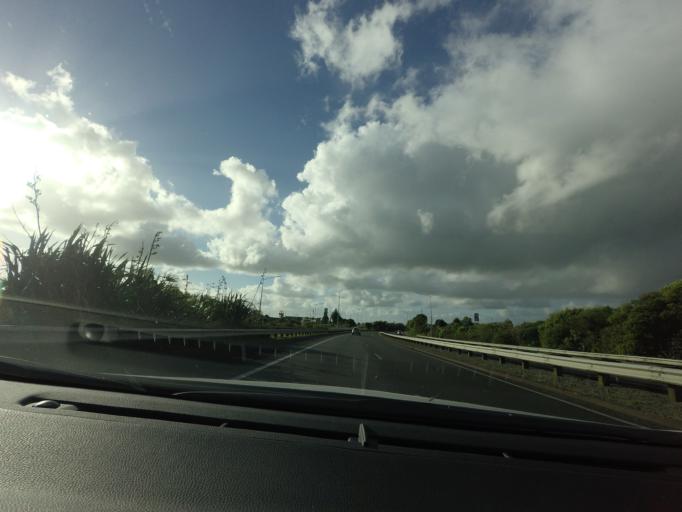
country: NZ
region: Auckland
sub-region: Auckland
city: Pukekohe East
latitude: -37.1951
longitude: 174.9843
